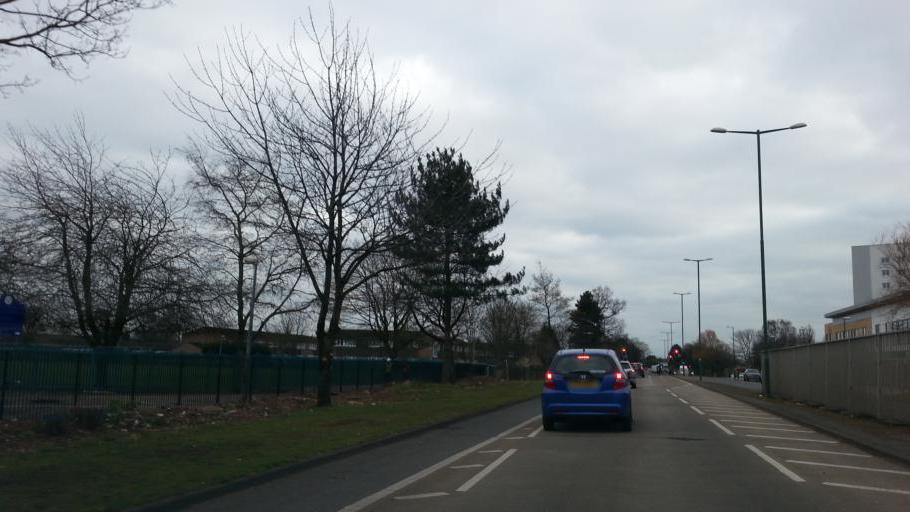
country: GB
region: England
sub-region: Solihull
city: Chelmsley Wood
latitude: 52.4795
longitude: -1.7273
